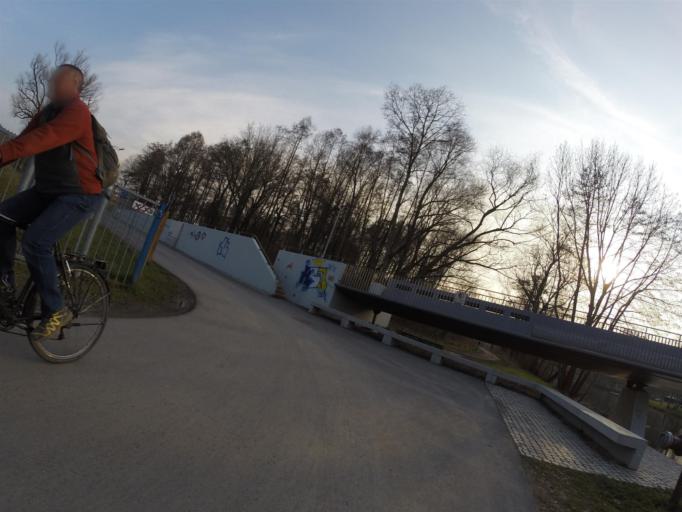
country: DE
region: Thuringia
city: Jena
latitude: 50.9150
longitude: 11.5809
